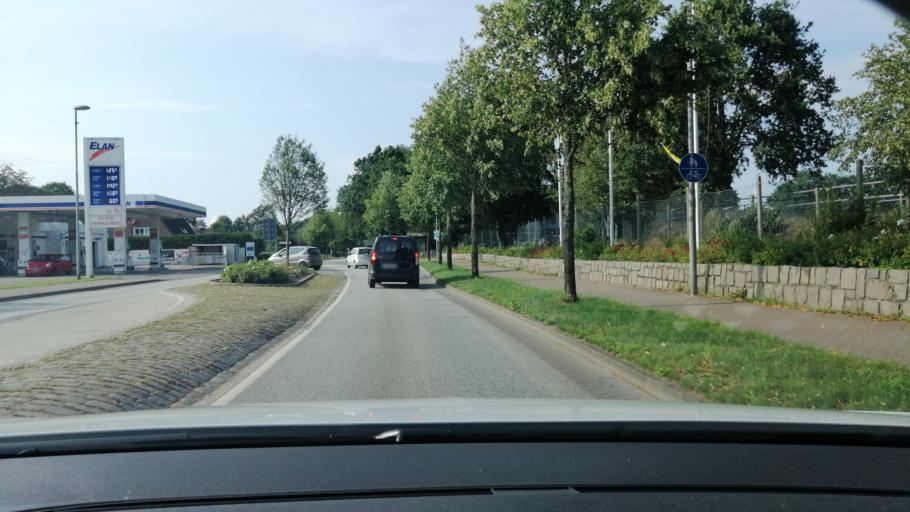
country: DE
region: Schleswig-Holstein
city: Leck
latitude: 54.7651
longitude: 8.9797
